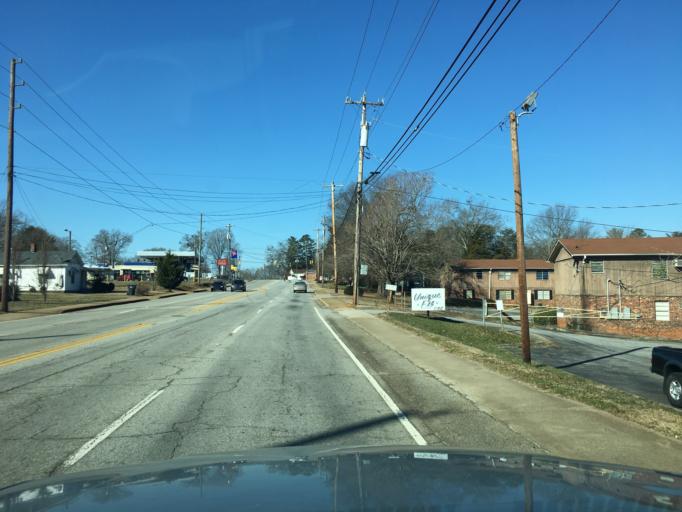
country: US
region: South Carolina
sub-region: Greenville County
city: Sans Souci
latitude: 34.8939
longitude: -82.4296
